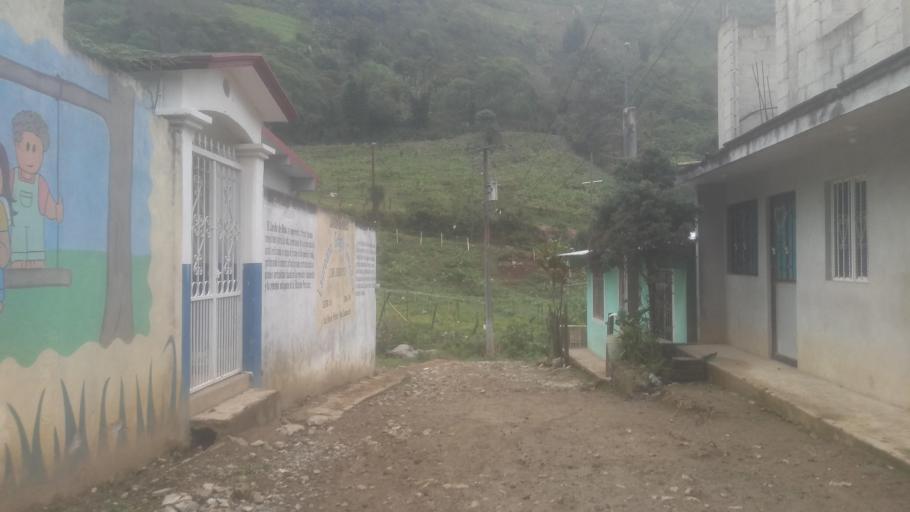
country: MX
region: Veracruz
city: Chocaman
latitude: 18.9964
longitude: -97.0592
